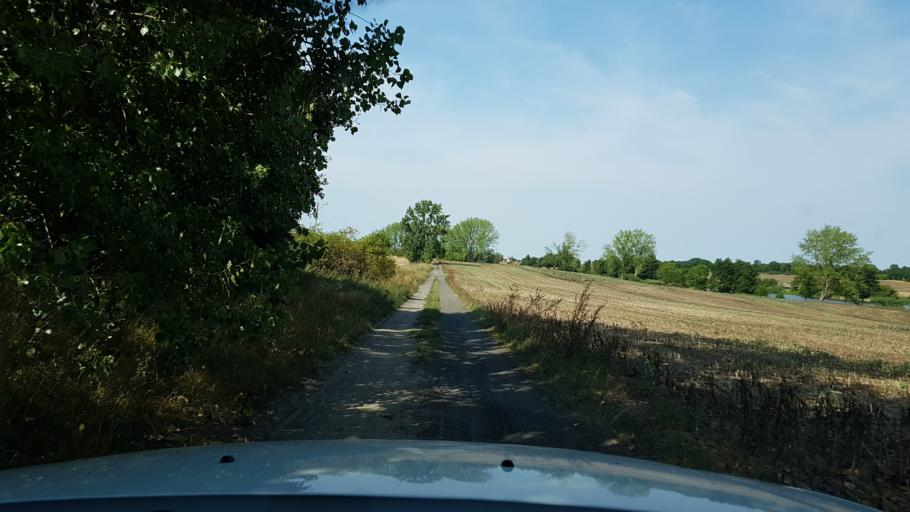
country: PL
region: West Pomeranian Voivodeship
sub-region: Powiat pyrzycki
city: Pyrzyce
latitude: 53.1151
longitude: 14.8850
